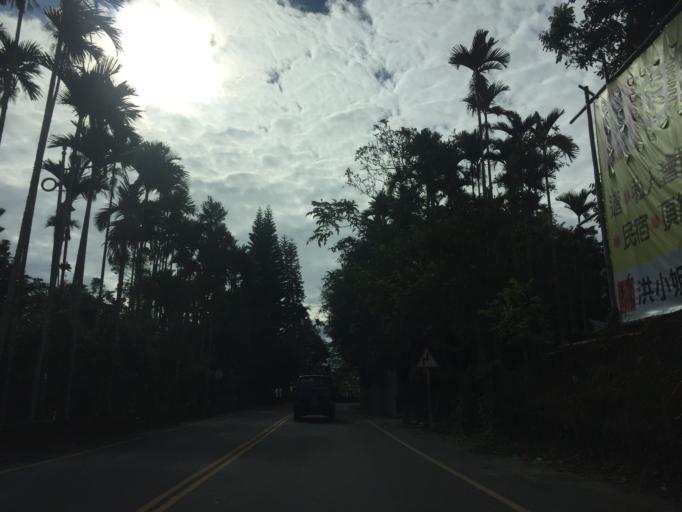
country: TW
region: Taiwan
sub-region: Nantou
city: Puli
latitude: 23.8646
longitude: 120.9036
